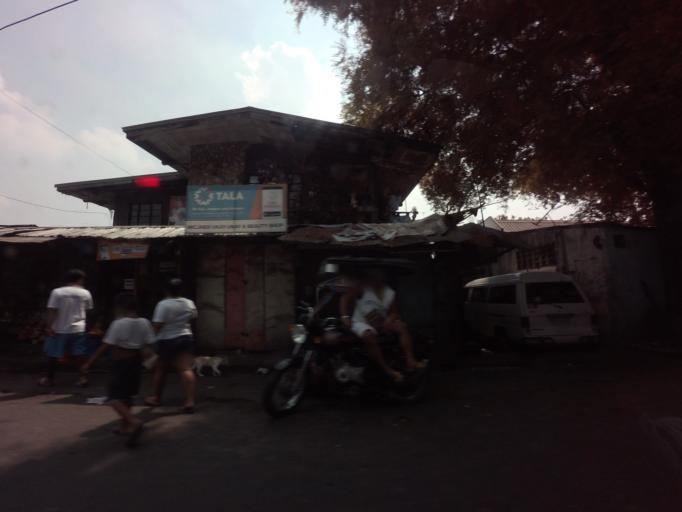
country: PH
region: Calabarzon
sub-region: Province of Rizal
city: Taguig
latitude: 14.5276
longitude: 121.0739
